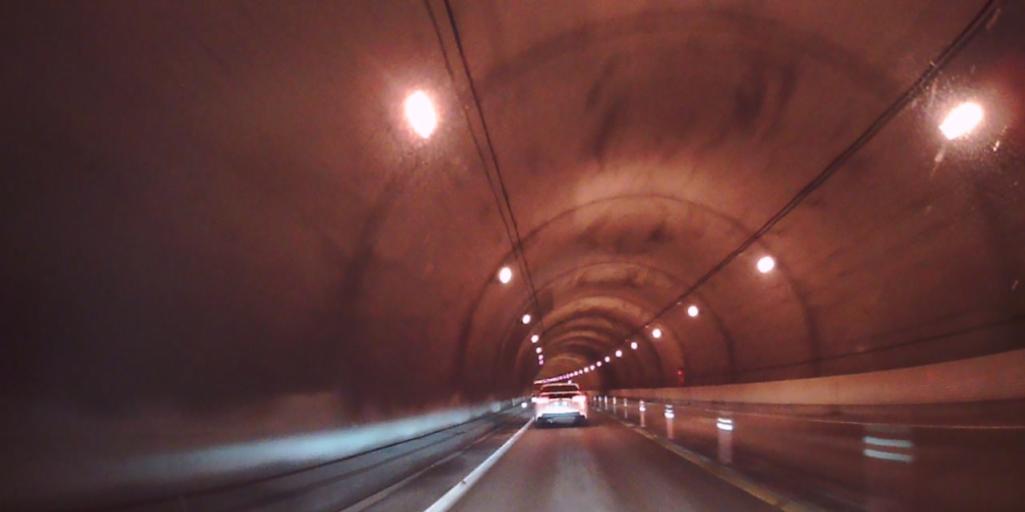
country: JP
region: Hokkaido
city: Date
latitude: 42.5543
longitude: 140.7845
